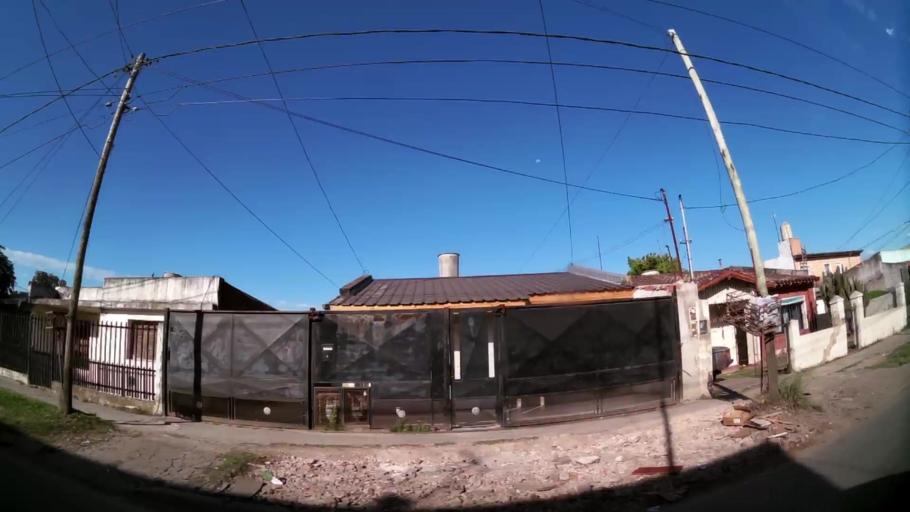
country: AR
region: Buenos Aires
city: Santa Catalina - Dique Lujan
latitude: -34.4982
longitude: -58.7285
